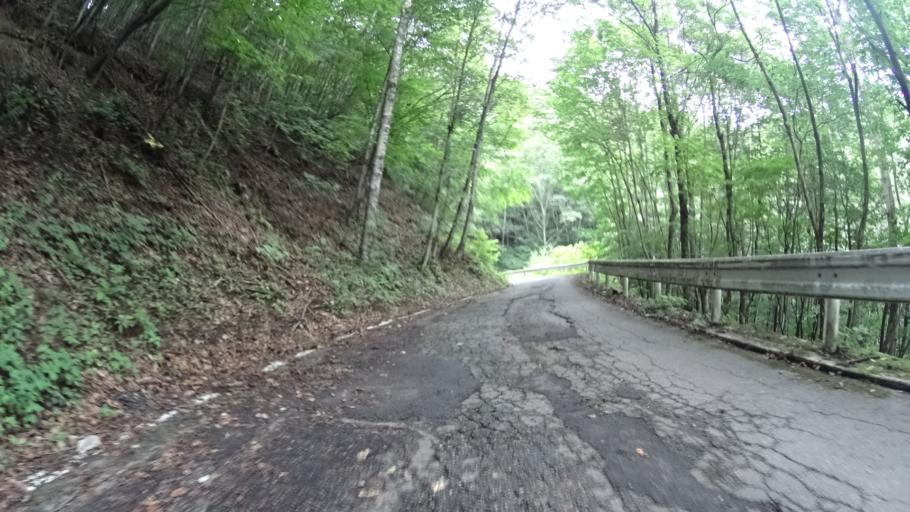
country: JP
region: Nagano
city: Saku
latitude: 36.0680
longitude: 138.6507
